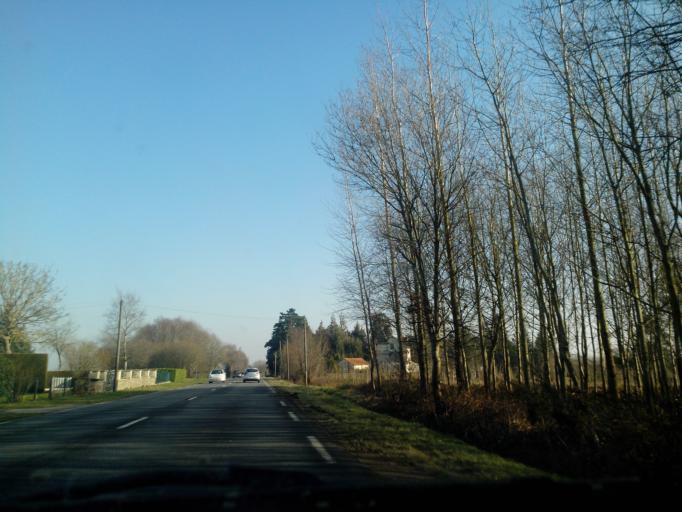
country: FR
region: Brittany
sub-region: Departement des Cotes-d'Armor
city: Merdrignac
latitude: 48.1941
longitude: -2.4505
